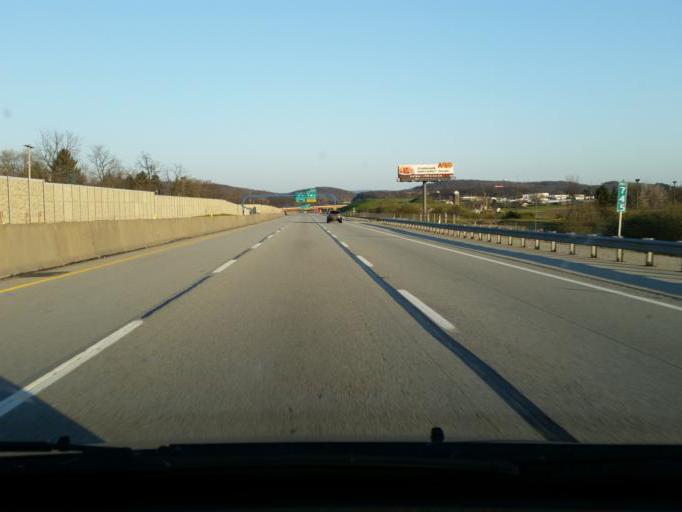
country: US
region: Pennsylvania
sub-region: Westmoreland County
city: New Stanton
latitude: 40.2311
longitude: -79.6173
